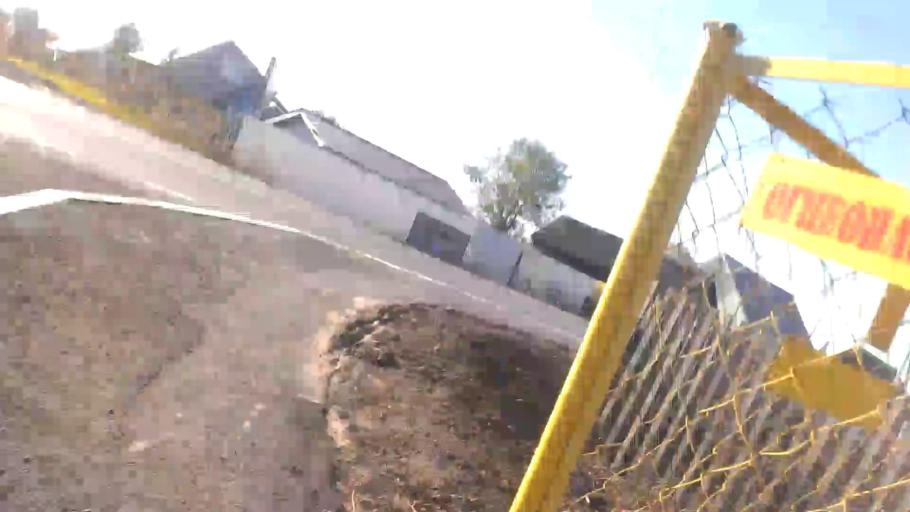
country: RU
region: Altai Krai
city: Sannikovo
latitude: 53.3139
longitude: 83.9619
